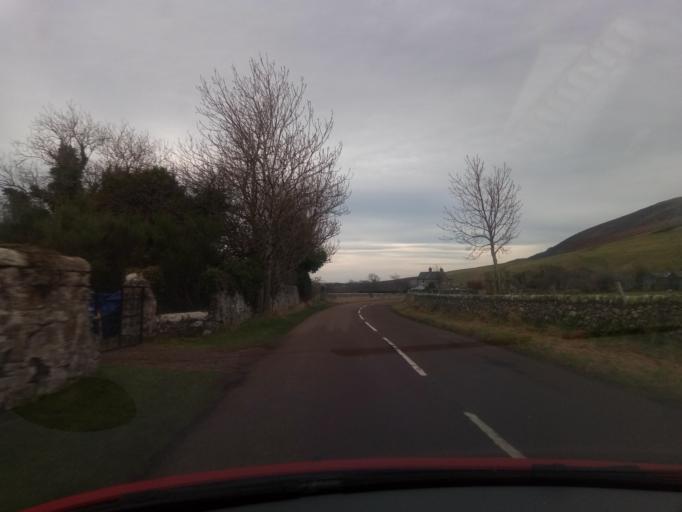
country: GB
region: England
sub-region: Northumberland
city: Kirknewton
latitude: 55.5673
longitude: -2.1430
